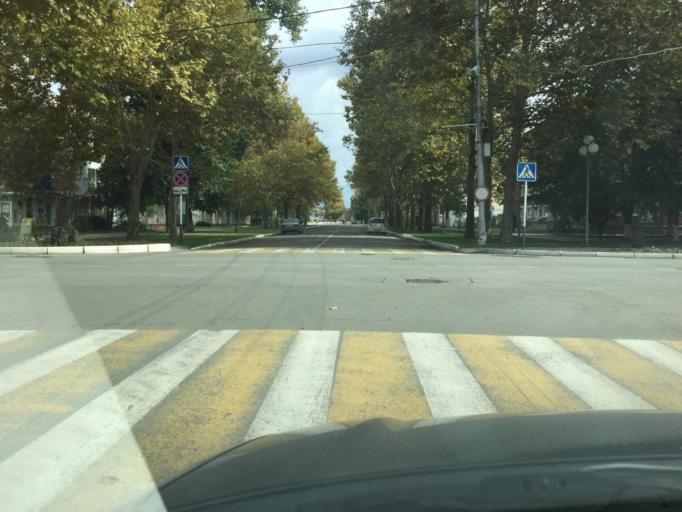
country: RU
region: Krasnodarskiy
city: Slavyansk-na-Kubani
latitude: 45.2575
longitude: 38.1213
